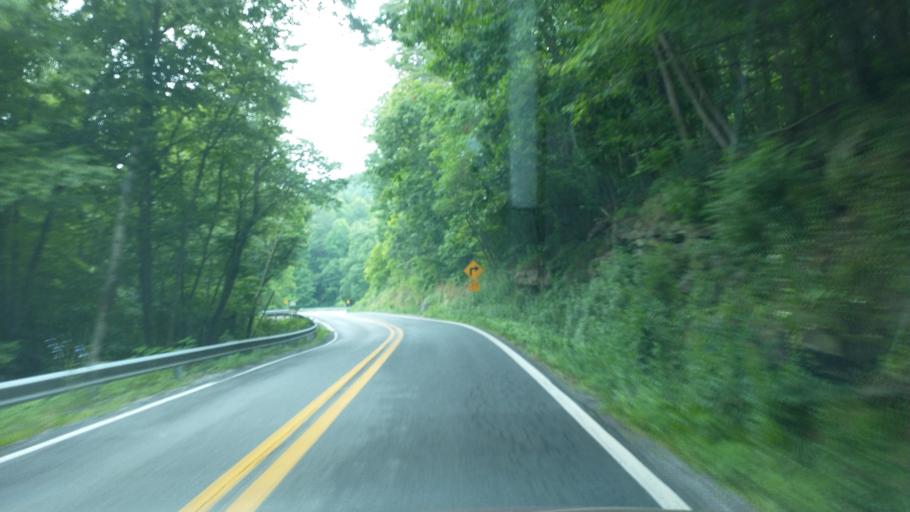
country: US
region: West Virginia
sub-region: Mercer County
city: Athens
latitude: 37.4152
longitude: -81.0517
